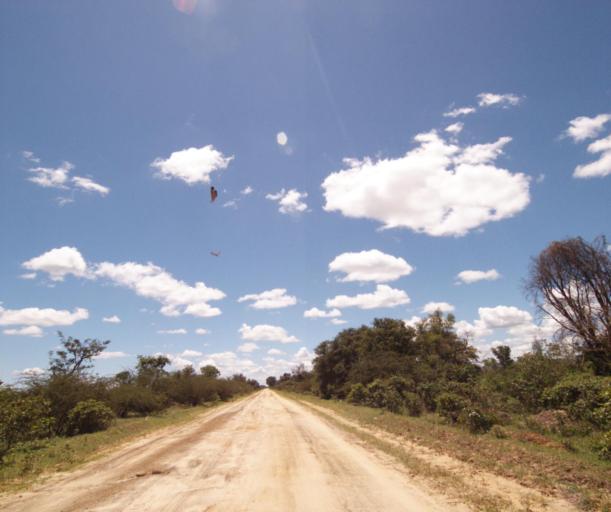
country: BR
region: Bahia
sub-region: Carinhanha
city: Carinhanha
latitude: -14.2095
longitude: -43.9887
